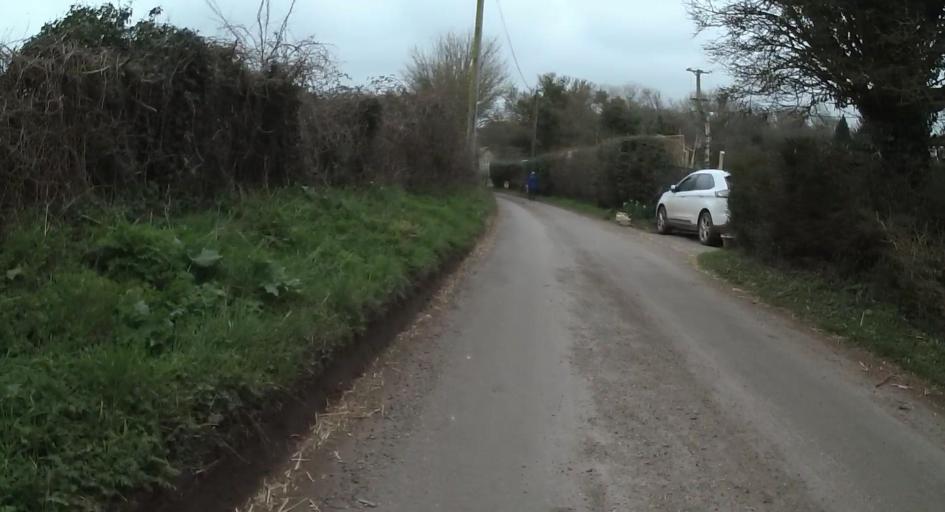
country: GB
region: England
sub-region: Hampshire
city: Four Marks
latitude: 51.0990
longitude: -1.1079
